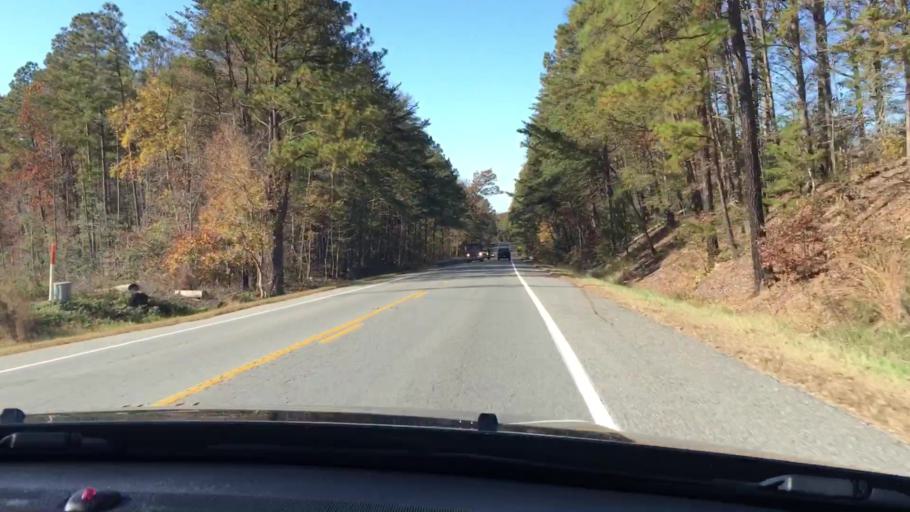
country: US
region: Virginia
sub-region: Hanover County
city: Hanover
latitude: 37.8386
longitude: -77.3774
